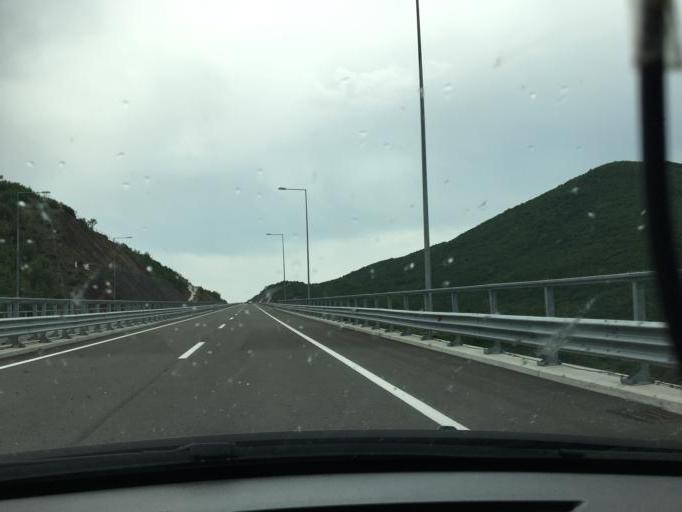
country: MK
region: Gevgelija
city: Miravci
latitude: 41.3456
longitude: 22.3740
